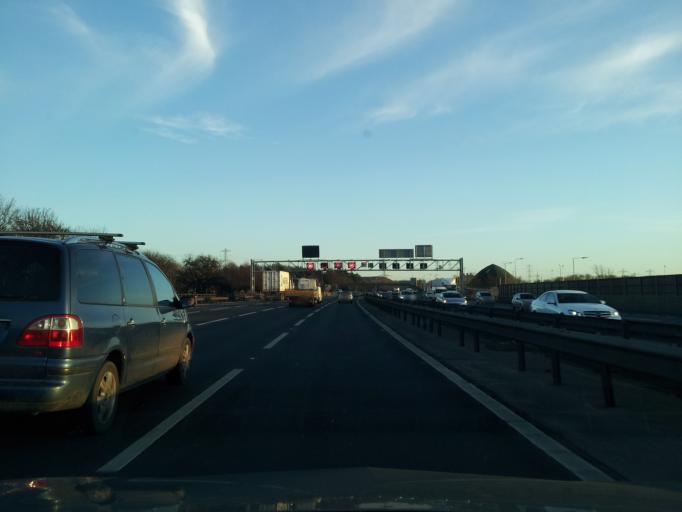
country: GB
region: England
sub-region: Central Bedfordshire
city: Harlington
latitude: 51.9502
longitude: -0.5050
